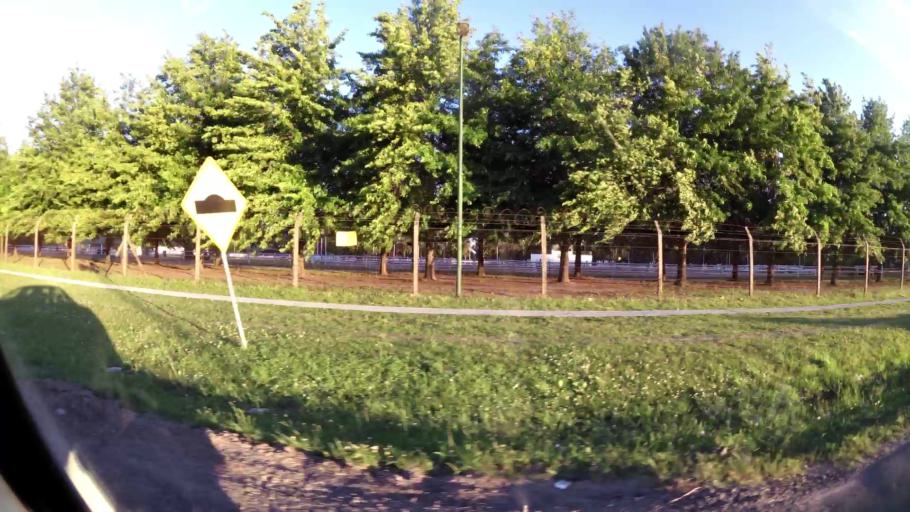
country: AR
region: Buenos Aires
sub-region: Partido de Quilmes
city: Quilmes
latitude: -34.8001
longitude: -58.1629
